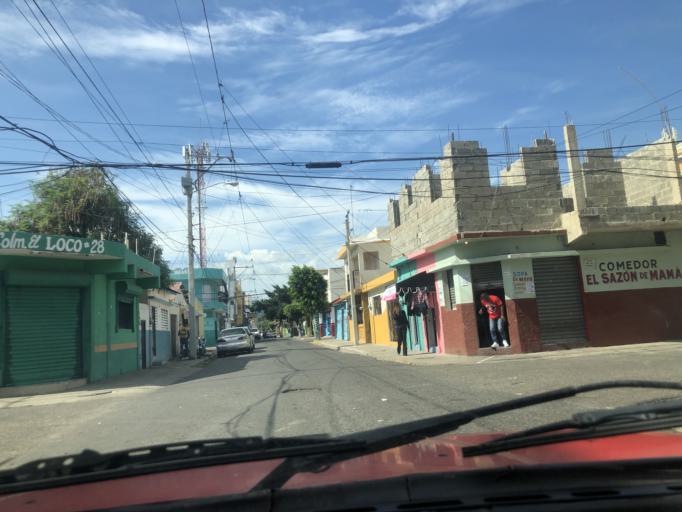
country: DO
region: Santiago
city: Santiago de los Caballeros
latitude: 19.4594
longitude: -70.7086
